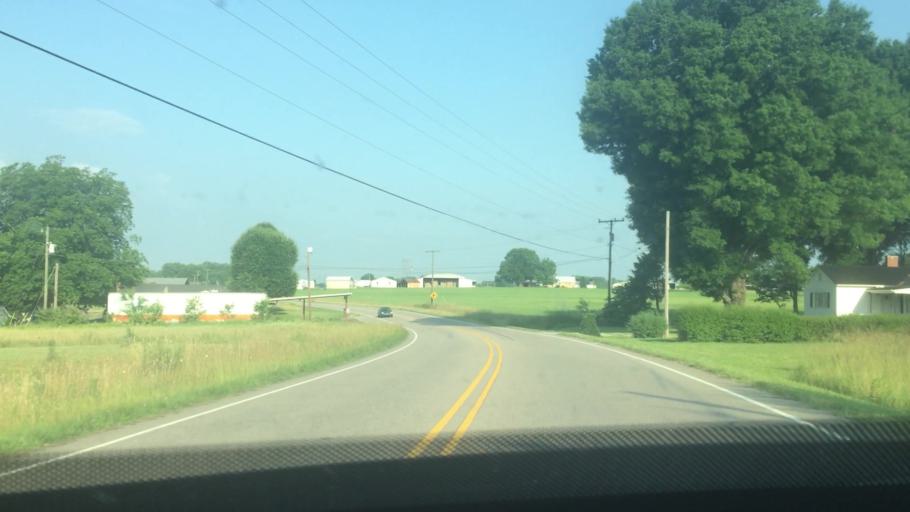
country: US
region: North Carolina
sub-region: Rowan County
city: Enochville
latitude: 35.5821
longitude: -80.7226
